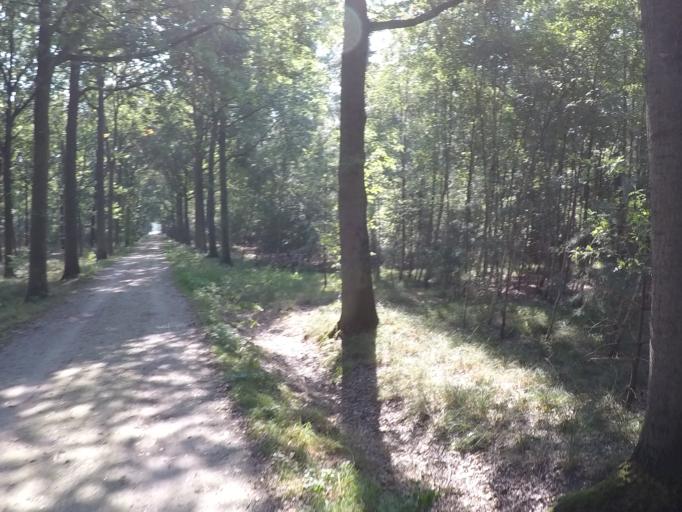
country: BE
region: Flanders
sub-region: Provincie Antwerpen
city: Kapellen
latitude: 51.3441
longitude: 4.4228
